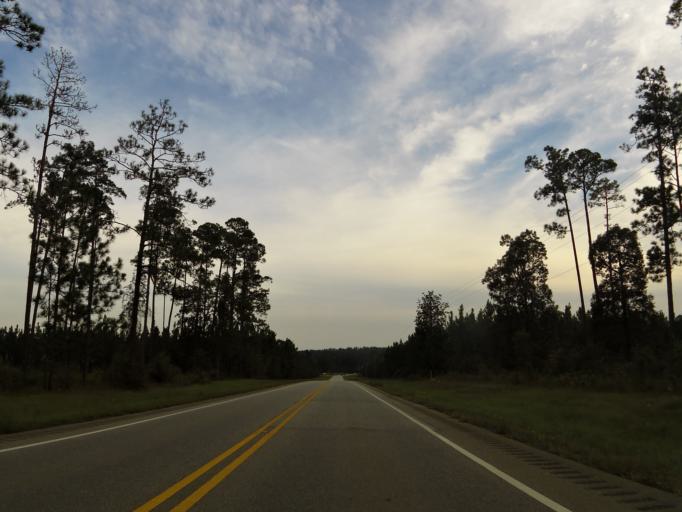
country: US
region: Alabama
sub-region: Monroe County
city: Frisco City
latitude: 31.2641
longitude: -87.4967
